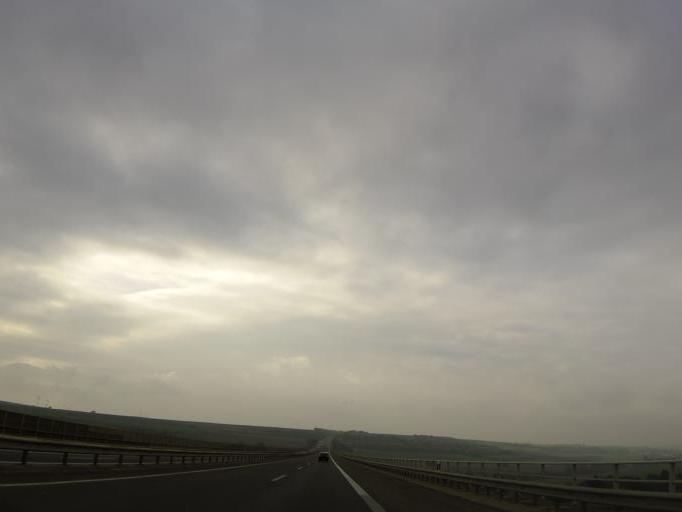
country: DE
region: Rheinland-Pfalz
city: Wahlheim
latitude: 49.7400
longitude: 8.0837
